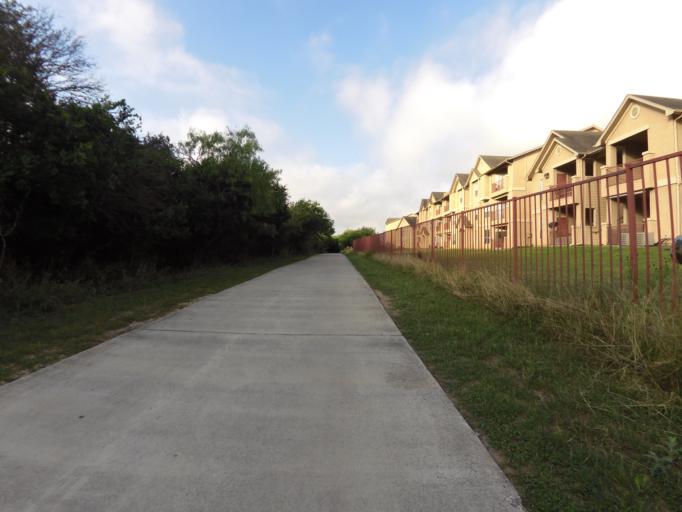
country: US
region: Texas
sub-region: Bexar County
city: Leon Valley
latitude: 29.5172
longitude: -98.6309
